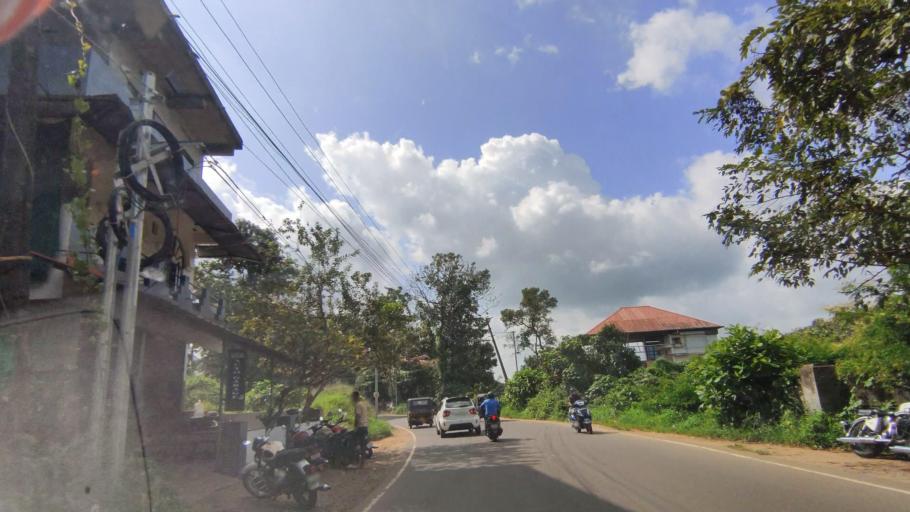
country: IN
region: Kerala
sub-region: Kottayam
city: Kottayam
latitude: 9.6707
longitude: 76.5549
